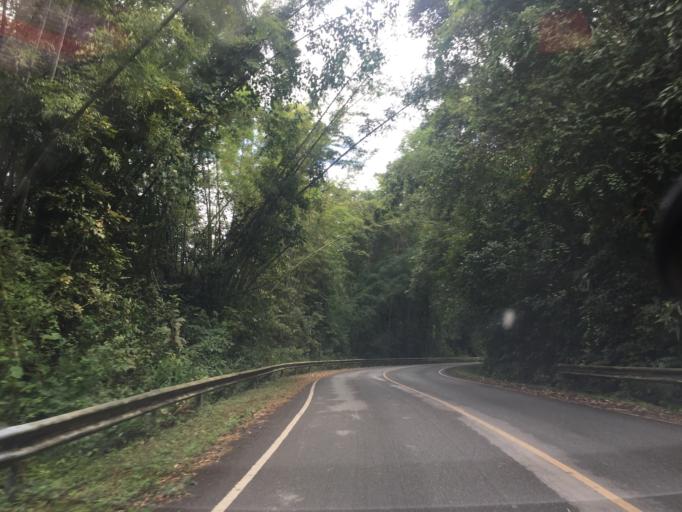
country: TH
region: Lampang
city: Mueang Pan
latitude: 18.8350
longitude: 99.4748
